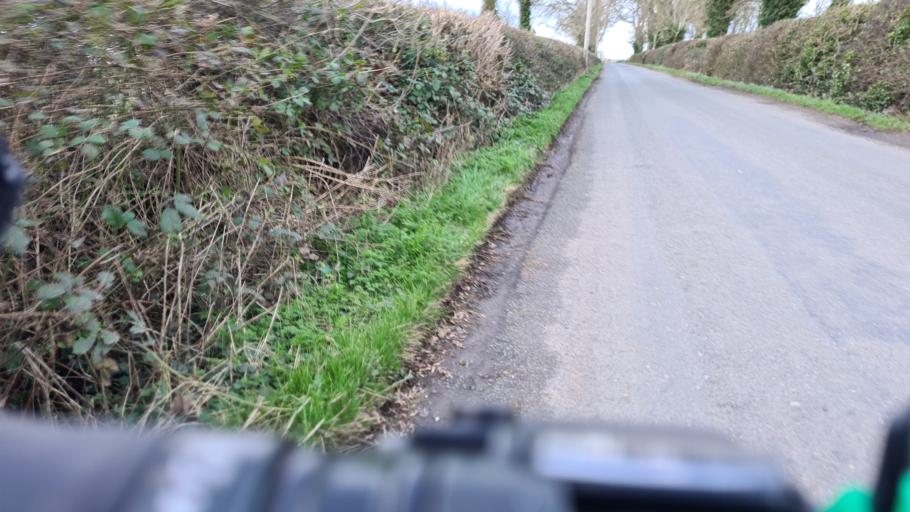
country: IE
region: Leinster
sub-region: Kildare
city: Celbridge
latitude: 53.3476
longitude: -6.5754
